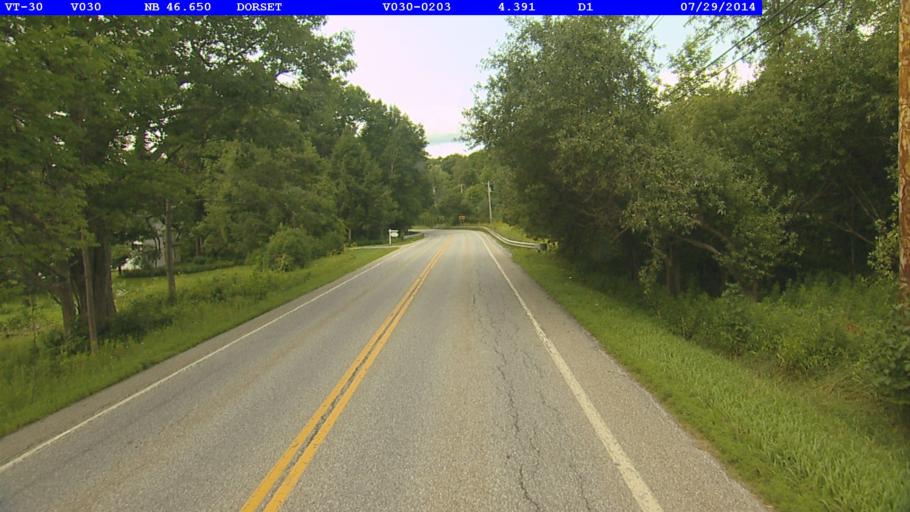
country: US
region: Vermont
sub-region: Bennington County
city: Manchester Center
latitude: 43.2677
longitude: -73.1082
